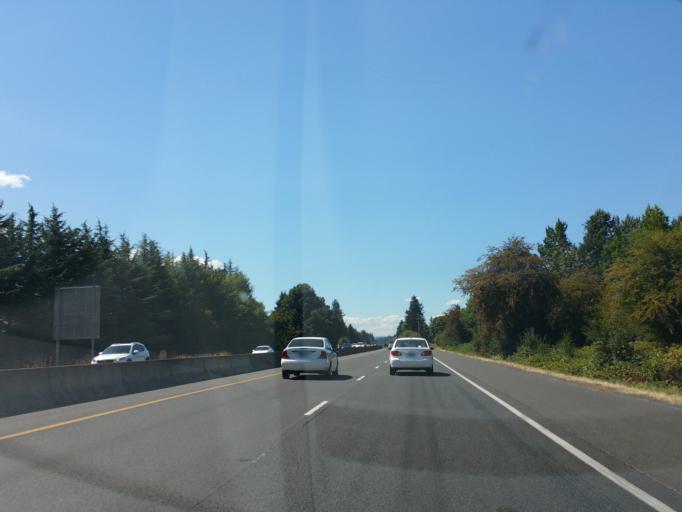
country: US
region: Washington
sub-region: Clark County
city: Mill Plain
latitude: 45.5967
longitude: -122.5221
